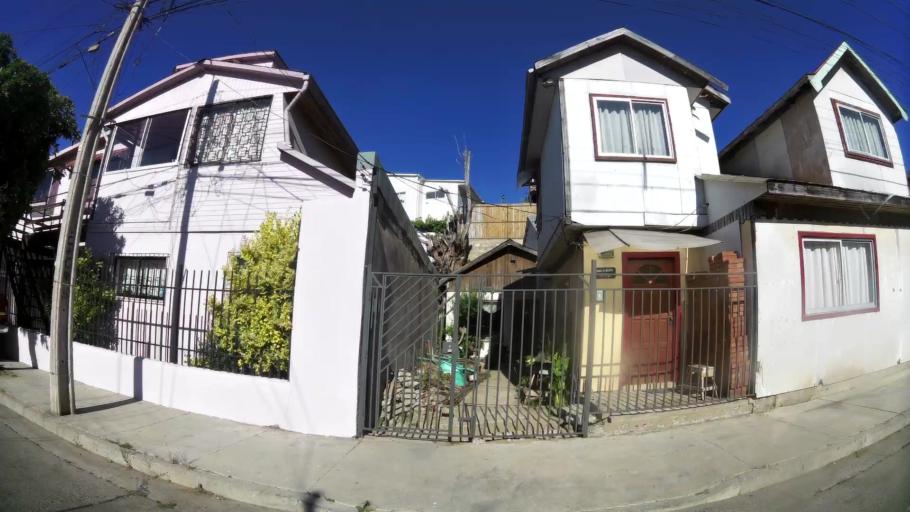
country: CL
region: Valparaiso
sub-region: Provincia de Valparaiso
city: Valparaiso
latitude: -33.0560
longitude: -71.6185
